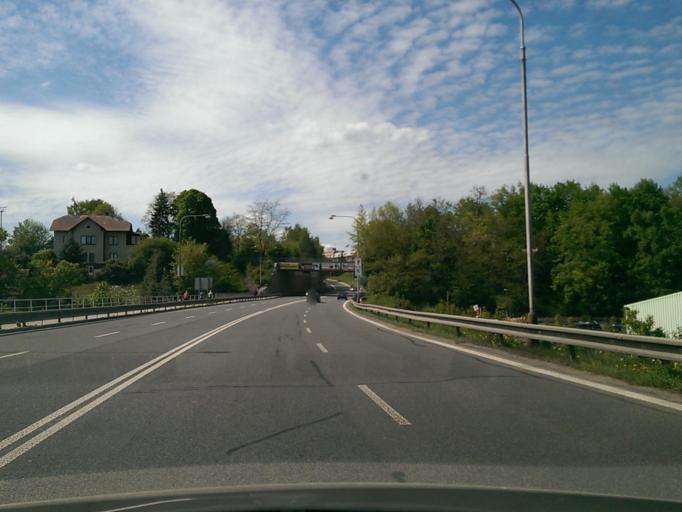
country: CZ
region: Liberecky
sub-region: Okres Semily
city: Turnov
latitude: 50.5855
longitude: 15.1473
